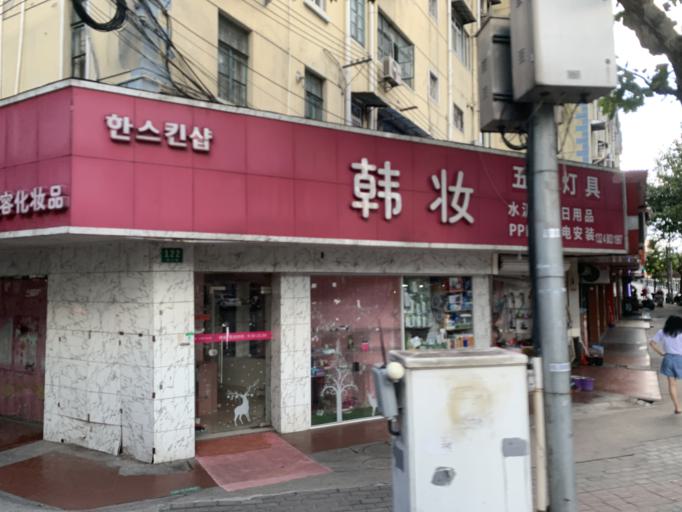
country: CN
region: Shanghai Shi
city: Pudong
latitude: 31.2490
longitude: 121.5468
